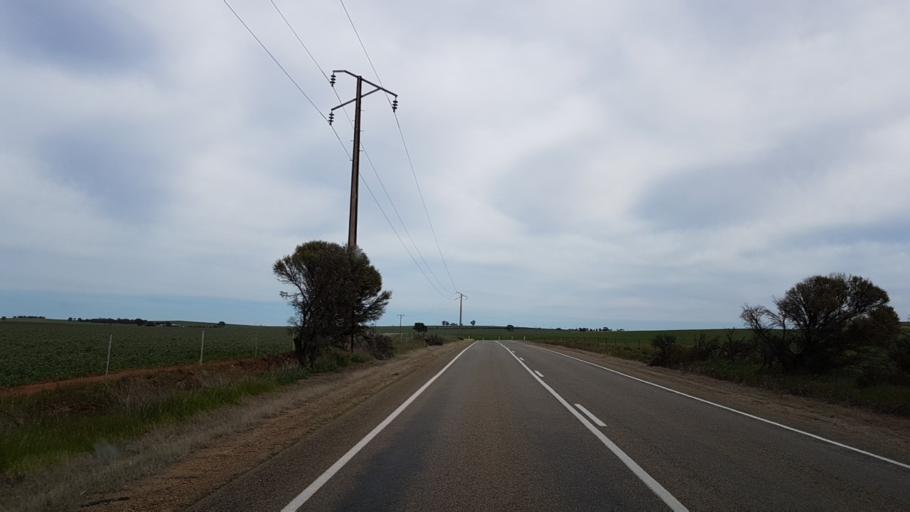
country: AU
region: South Australia
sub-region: Port Pirie City and Dists
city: Crystal Brook
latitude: -33.2706
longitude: 138.3180
